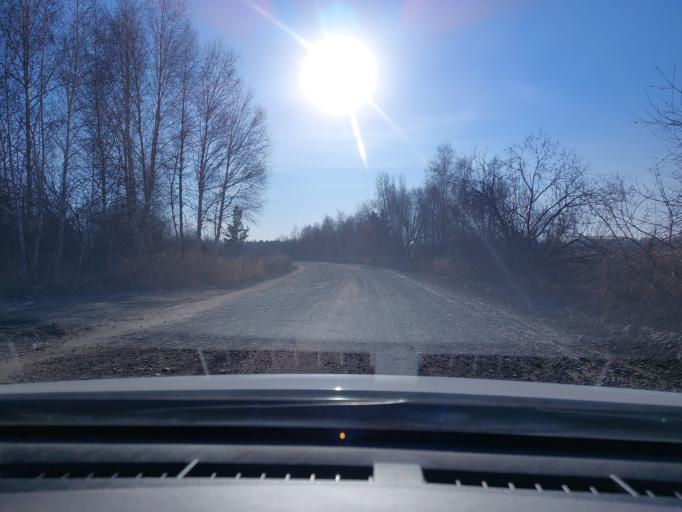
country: RU
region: Irkutsk
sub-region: Irkutskiy Rayon
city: Irkutsk
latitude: 52.3082
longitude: 104.2724
